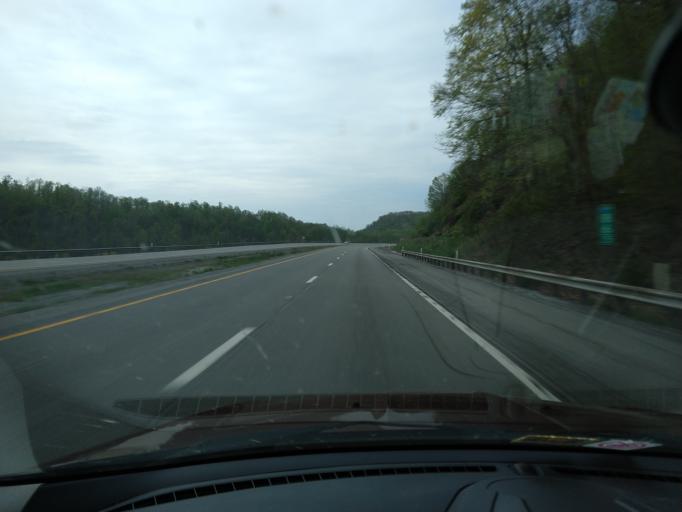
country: US
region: West Virginia
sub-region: Lewis County
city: Weston
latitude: 38.9186
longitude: -80.5584
